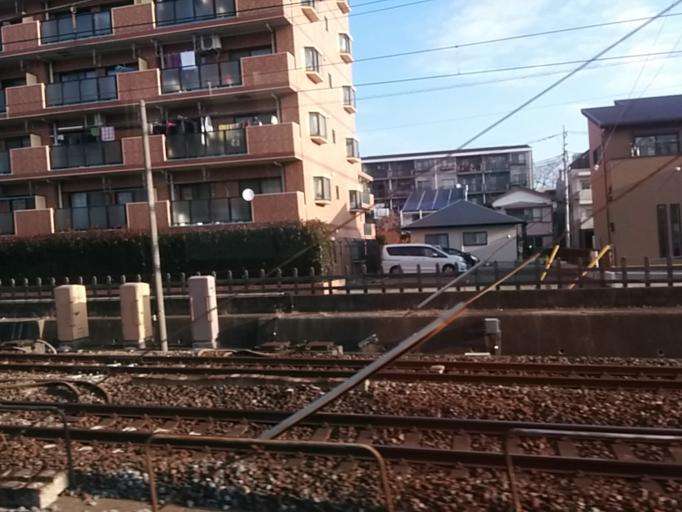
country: JP
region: Saitama
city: Shiki
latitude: 35.8164
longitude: 139.5842
